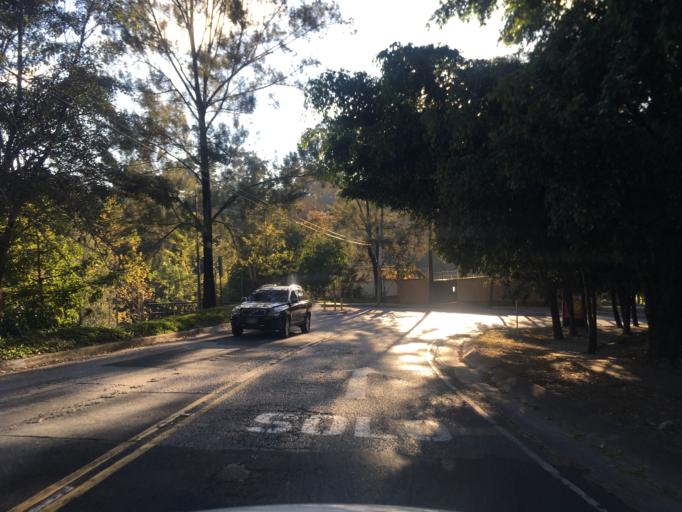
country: GT
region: Guatemala
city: Santa Catarina Pinula
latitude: 14.6043
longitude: -90.4925
